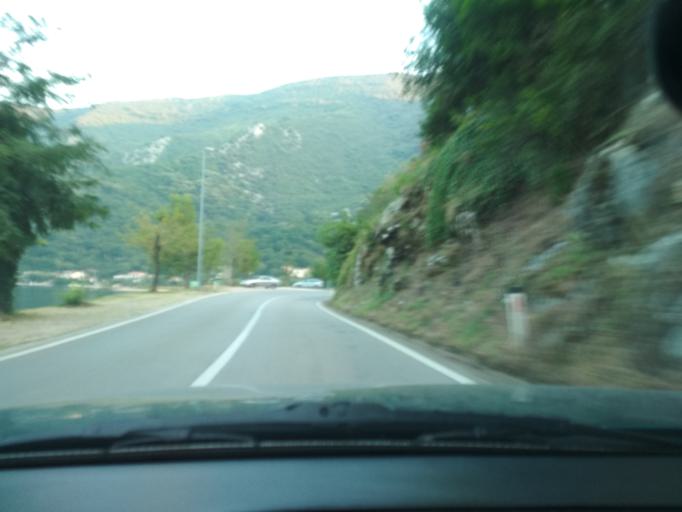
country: ME
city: Lipci
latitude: 42.4916
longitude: 18.6502
